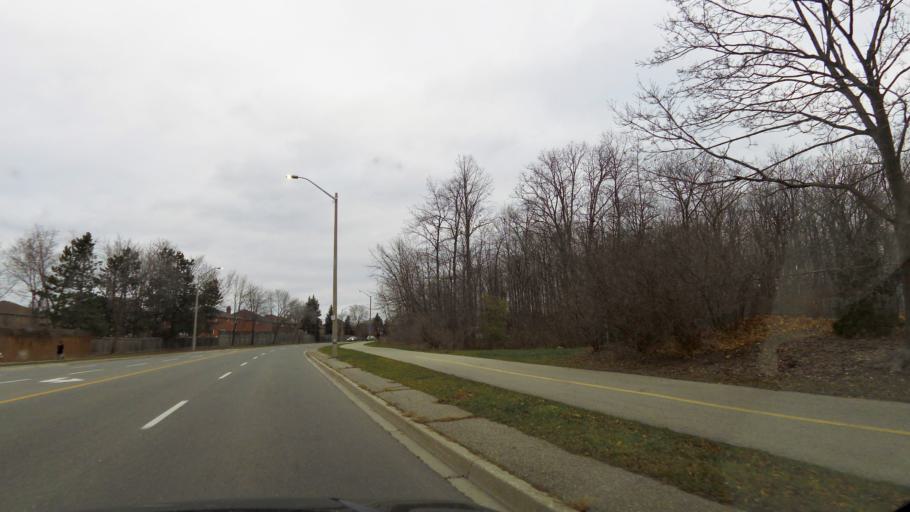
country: CA
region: Ontario
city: Mississauga
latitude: 43.5708
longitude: -79.6690
